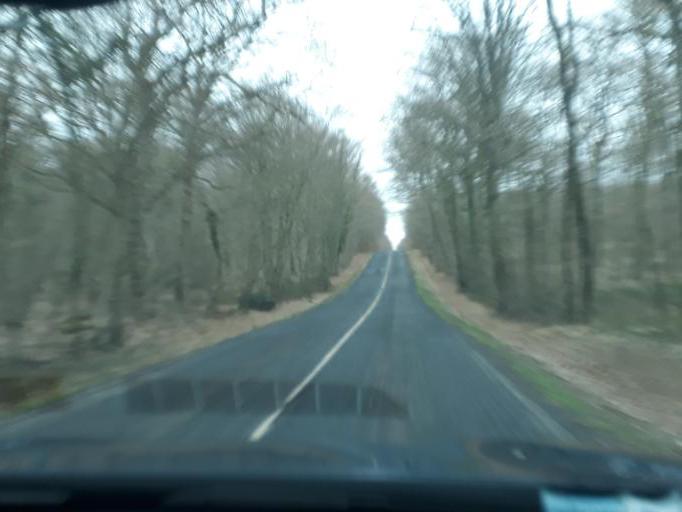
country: FR
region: Centre
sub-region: Departement du Loir-et-Cher
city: Ouzouer-le-Marche
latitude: 47.8323
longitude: 1.4244
